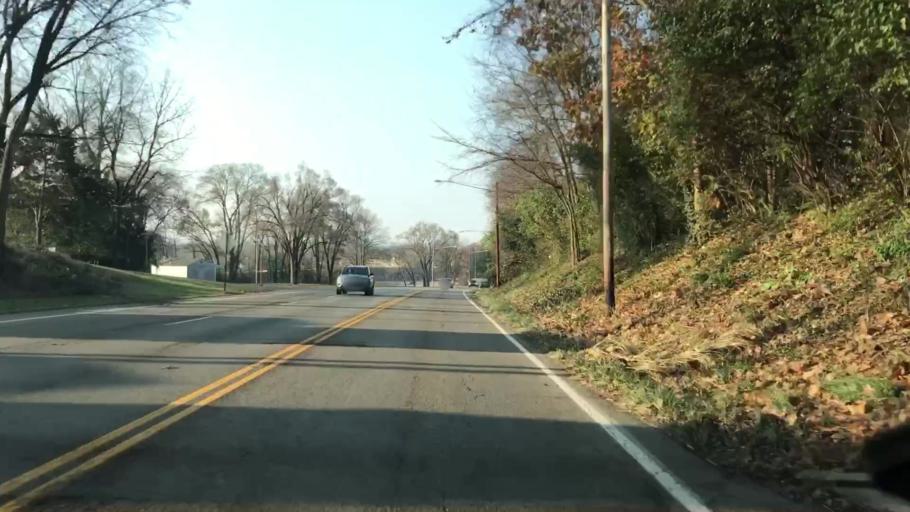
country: US
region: Ohio
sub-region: Greene County
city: Fairborn
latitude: 39.8361
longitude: -84.0108
